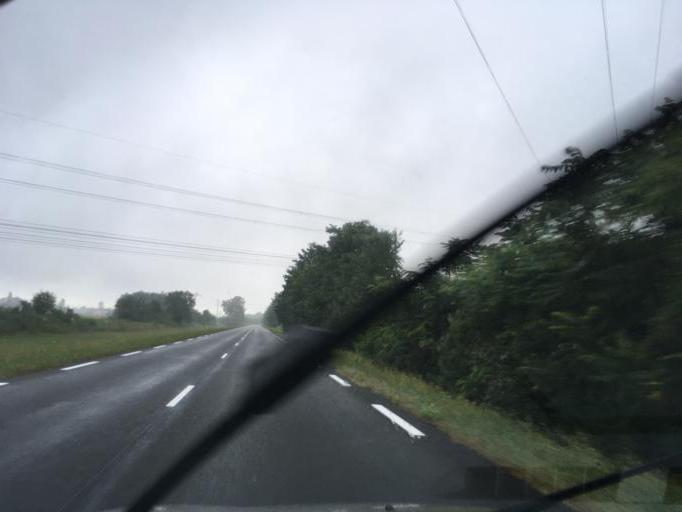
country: FR
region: Midi-Pyrenees
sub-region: Departement des Hautes-Pyrenees
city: Andrest
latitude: 43.3375
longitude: 0.0697
